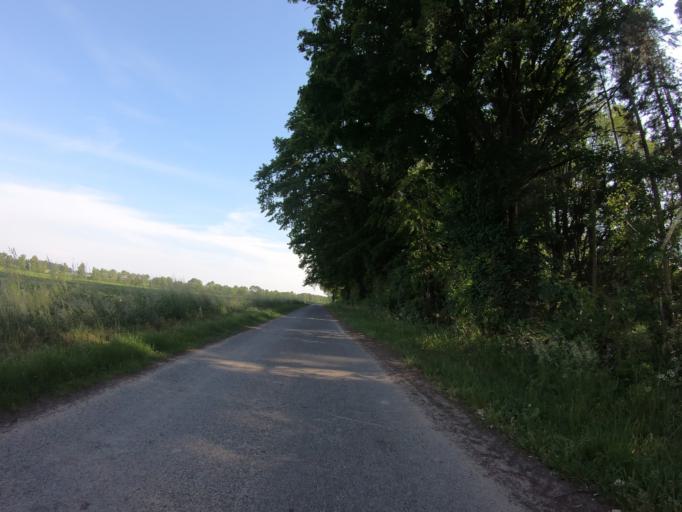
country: DE
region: Lower Saxony
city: Wasbuttel
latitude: 52.4008
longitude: 10.6064
